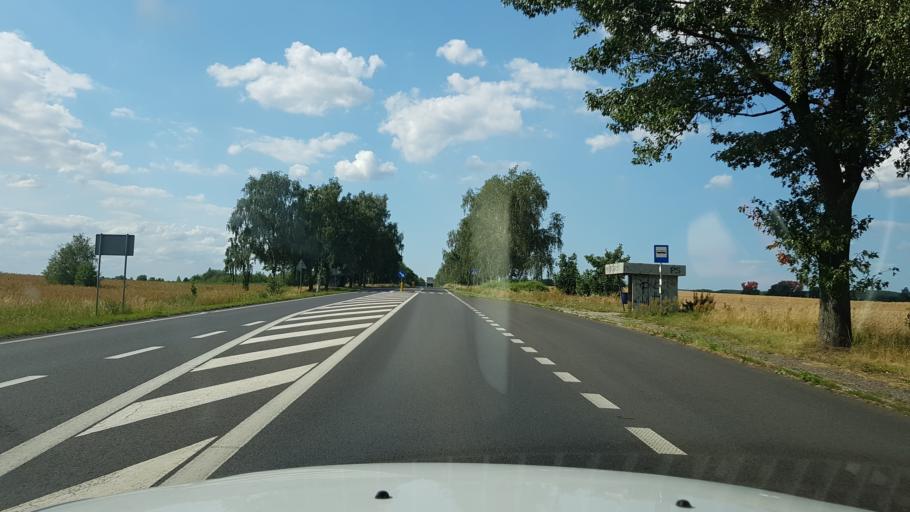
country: PL
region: West Pomeranian Voivodeship
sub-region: Powiat gryfinski
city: Stare Czarnowo
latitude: 53.2306
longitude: 14.7922
